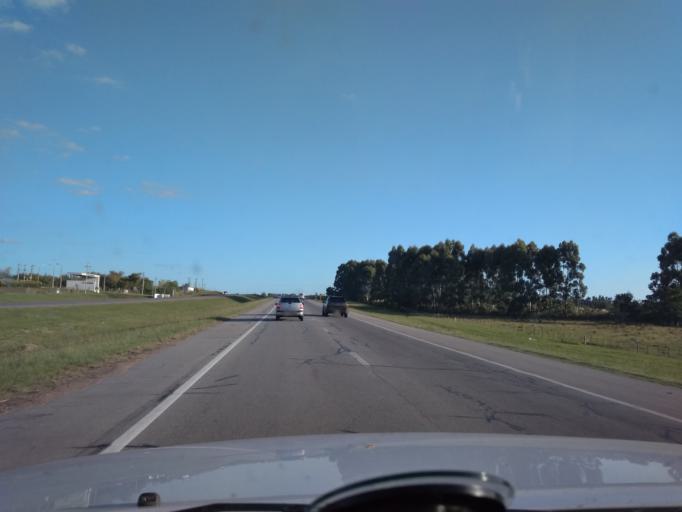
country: UY
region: Canelones
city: Progreso
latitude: -34.6797
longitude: -56.2409
